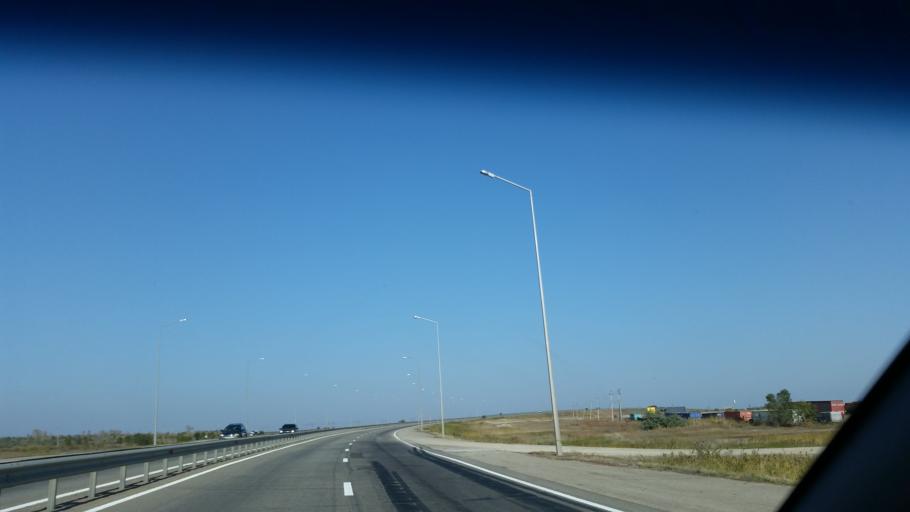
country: KZ
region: Astana Qalasy
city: Astana
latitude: 51.2467
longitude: 71.3378
